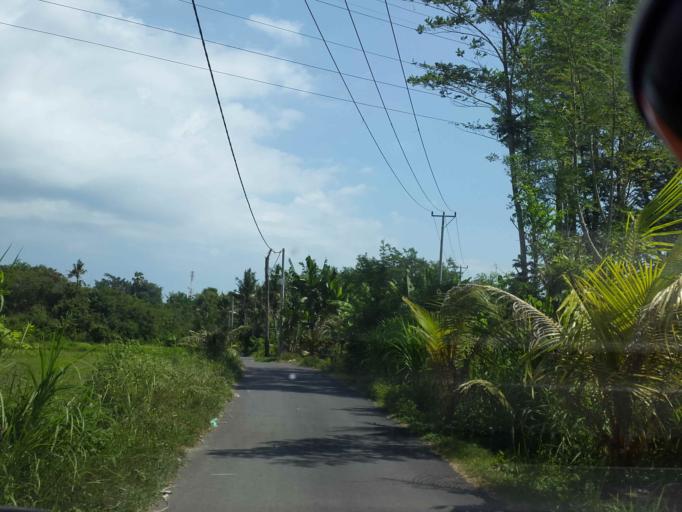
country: ID
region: Bali
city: Klungkung
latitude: -8.5625
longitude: 115.3810
